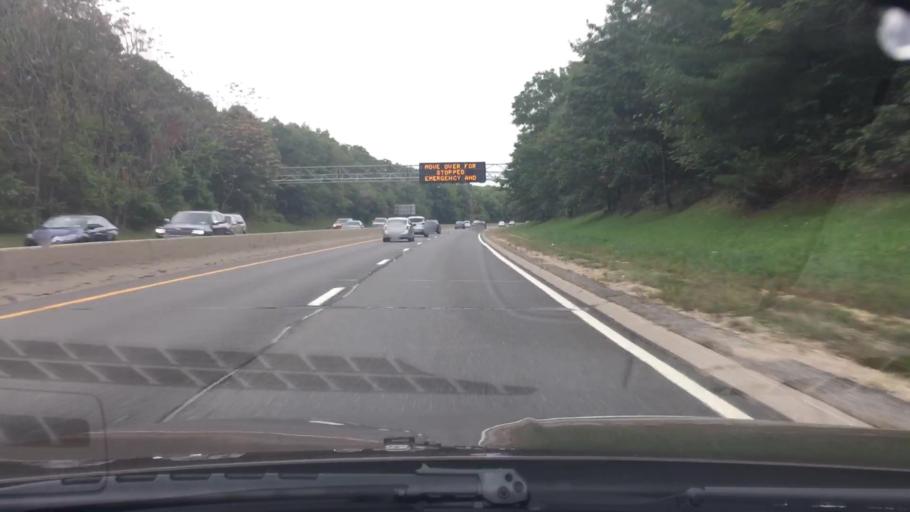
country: US
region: New York
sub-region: Suffolk County
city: West Hills
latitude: 40.8027
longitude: -73.4342
